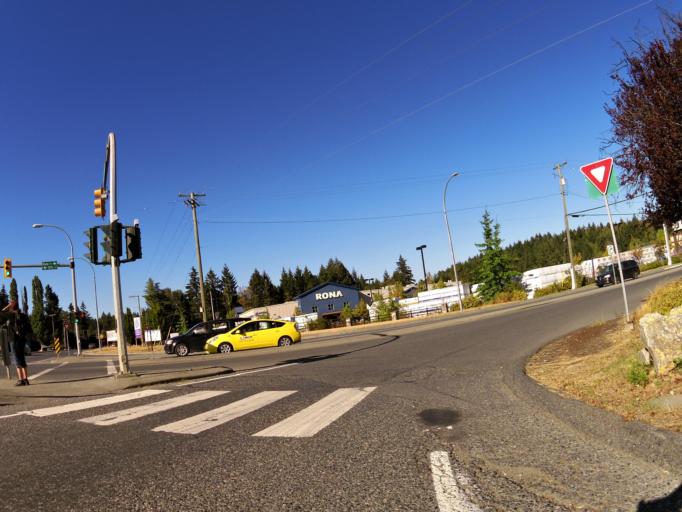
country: CA
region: British Columbia
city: Nanaimo
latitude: 49.1305
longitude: -123.9201
